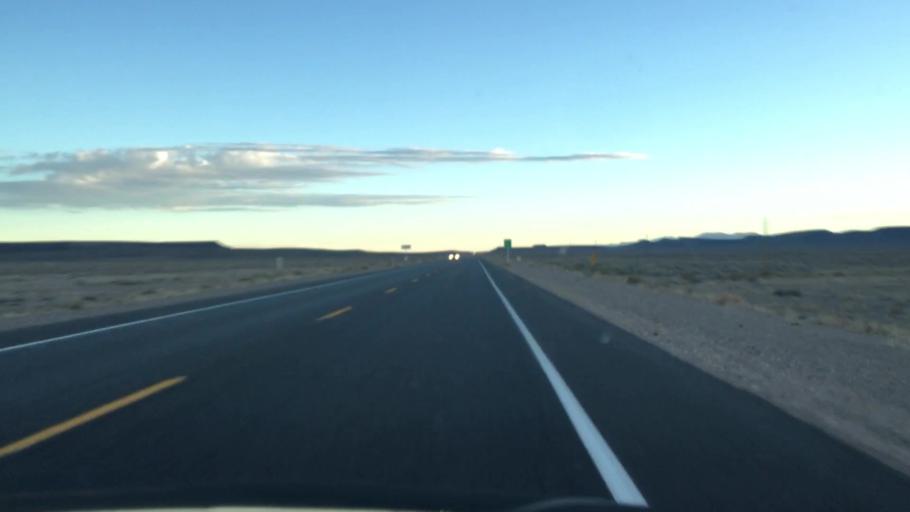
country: US
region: Nevada
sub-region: Esmeralda County
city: Goldfield
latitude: 37.4446
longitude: -117.1662
